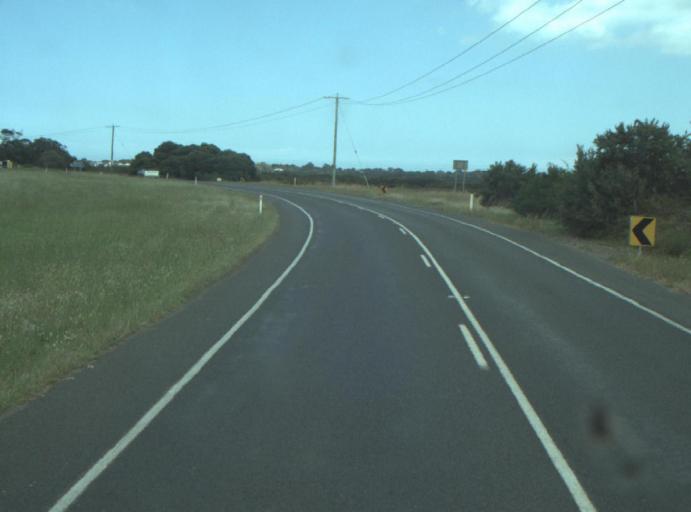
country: AU
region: Victoria
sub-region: Greater Geelong
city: Leopold
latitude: -38.2509
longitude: 144.5035
